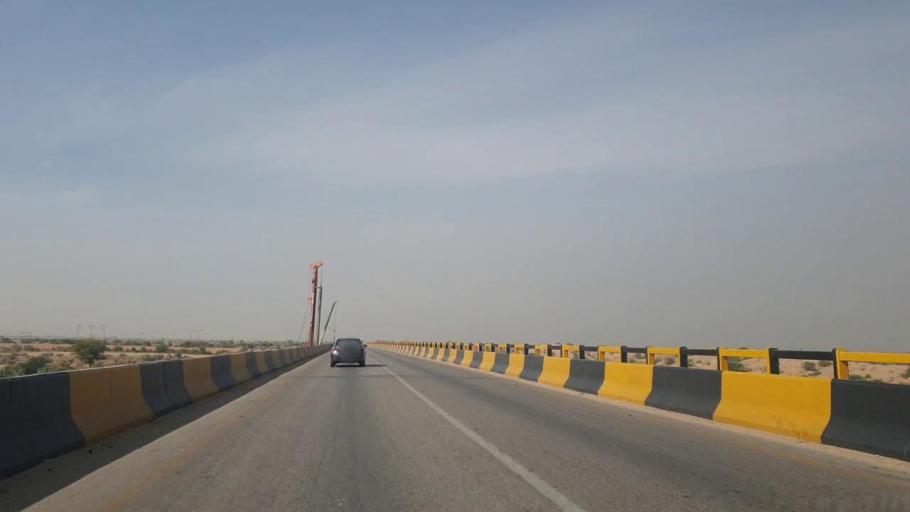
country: PK
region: Sindh
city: Sann
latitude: 26.0351
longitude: 68.1182
